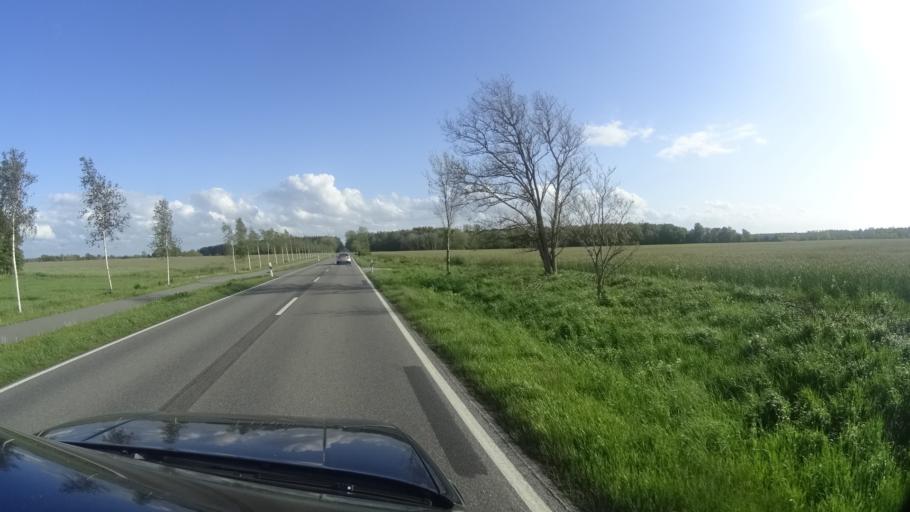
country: DE
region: Mecklenburg-Vorpommern
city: Ostseebad Dierhagen
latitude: 54.2849
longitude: 12.3547
